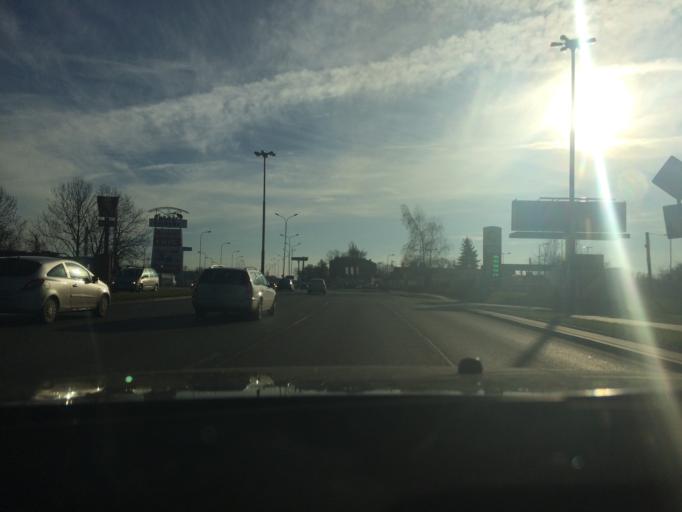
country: PL
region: Lodz Voivodeship
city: Lodz
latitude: 51.7519
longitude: 19.4362
